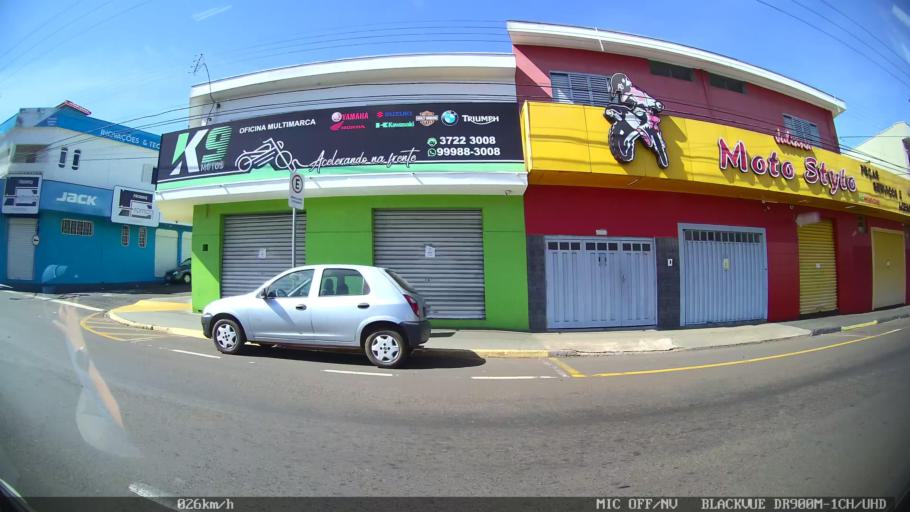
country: BR
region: Sao Paulo
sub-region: Franca
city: Franca
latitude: -20.5272
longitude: -47.4020
